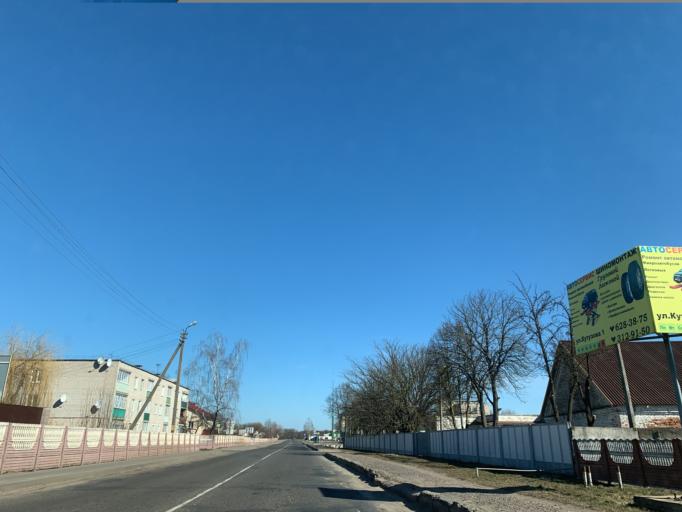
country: BY
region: Minsk
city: Nyasvizh
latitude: 53.2131
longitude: 26.6982
